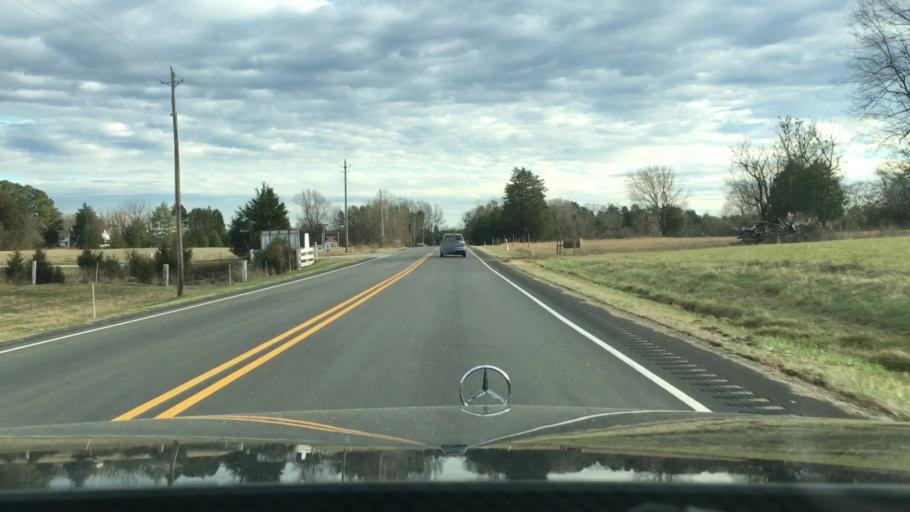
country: US
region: North Carolina
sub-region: Caswell County
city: Yanceyville
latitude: 36.3682
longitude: -79.2557
